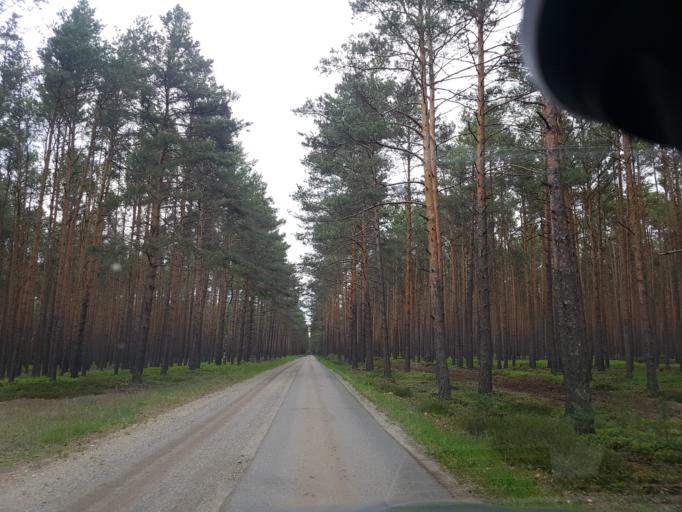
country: DE
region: Brandenburg
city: Crinitz
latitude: 51.6938
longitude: 13.7758
